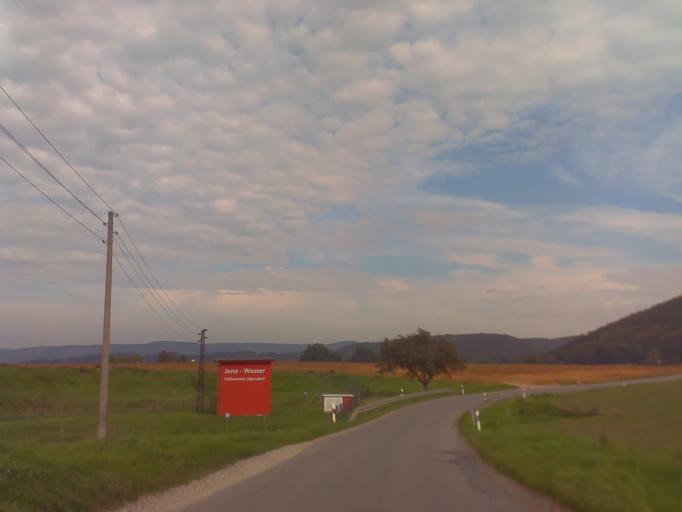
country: DE
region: Thuringia
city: Schops
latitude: 50.8362
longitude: 11.6064
